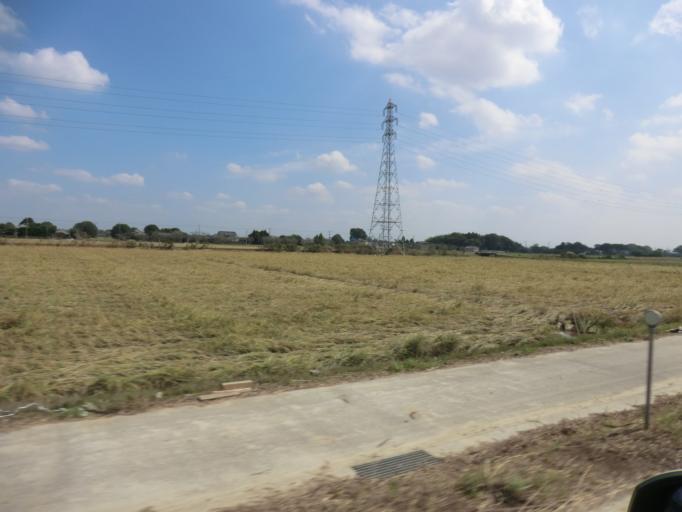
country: JP
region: Ibaraki
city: Ishige
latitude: 36.0727
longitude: 139.9881
